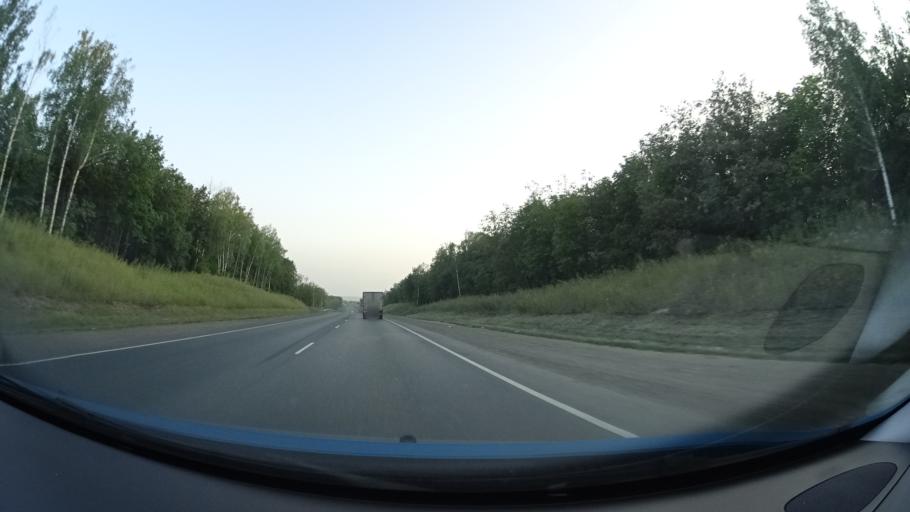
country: RU
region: Samara
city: Sernovodsk
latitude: 53.9234
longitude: 51.3133
